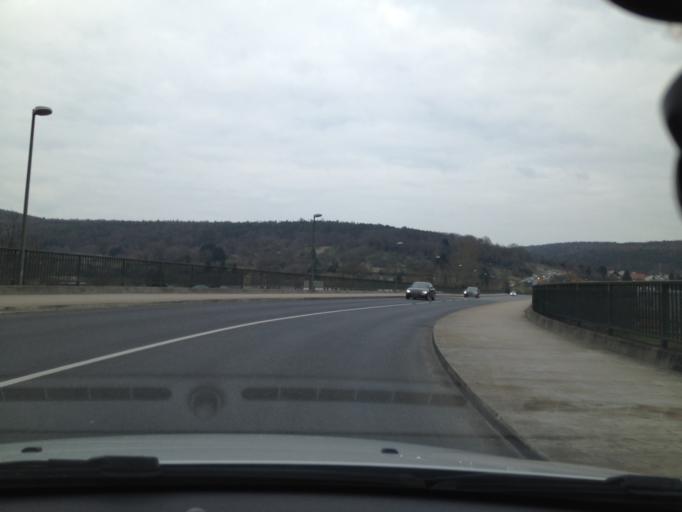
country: DE
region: Bavaria
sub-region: Regierungsbezirk Unterfranken
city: Kreuzwertheim
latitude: 49.7701
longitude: 9.5083
